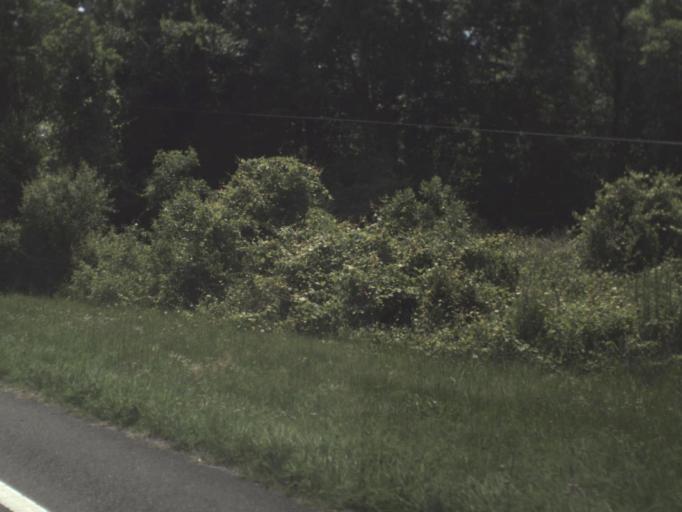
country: US
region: Florida
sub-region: Nassau County
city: Yulee
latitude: 30.5671
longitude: -81.6144
